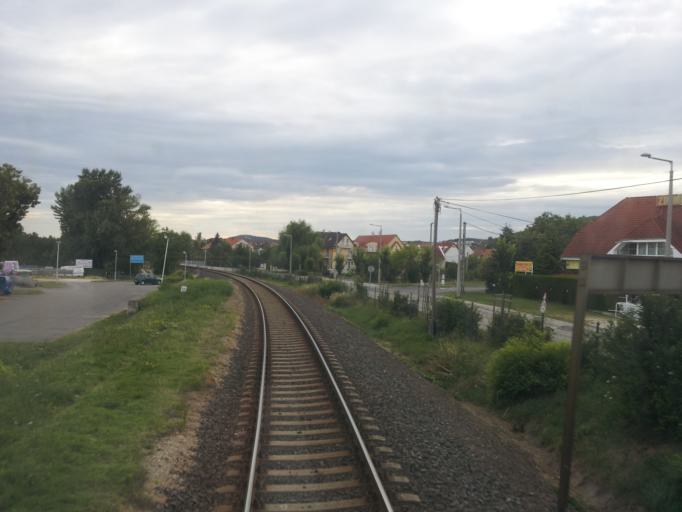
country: HU
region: Veszprem
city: Balatonfured
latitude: 46.9627
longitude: 17.8967
